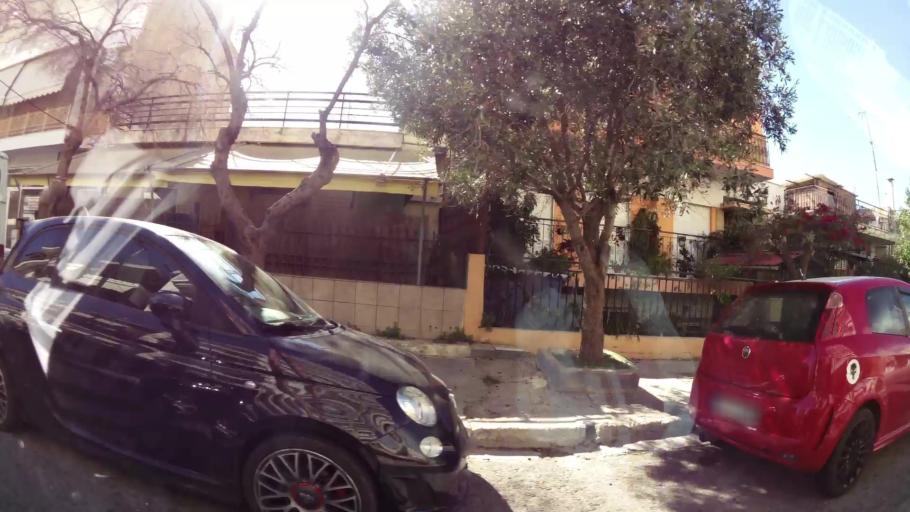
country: GR
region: Attica
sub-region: Nomos Piraios
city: Perama
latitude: 37.9673
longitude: 23.5701
